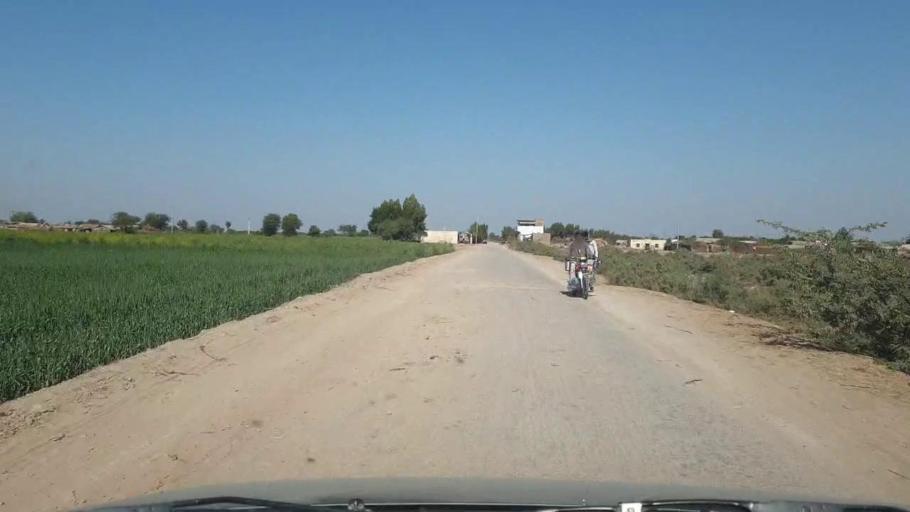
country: PK
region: Sindh
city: Samaro
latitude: 25.2955
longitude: 69.2629
